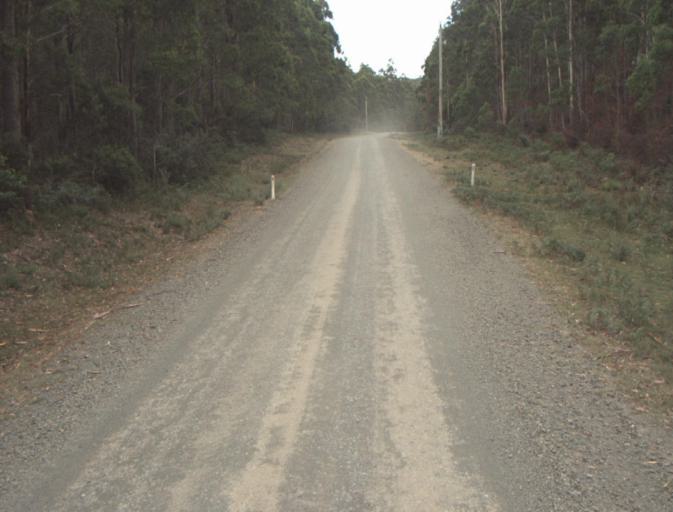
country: AU
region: Tasmania
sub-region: Dorset
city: Scottsdale
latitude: -41.4409
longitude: 147.5157
